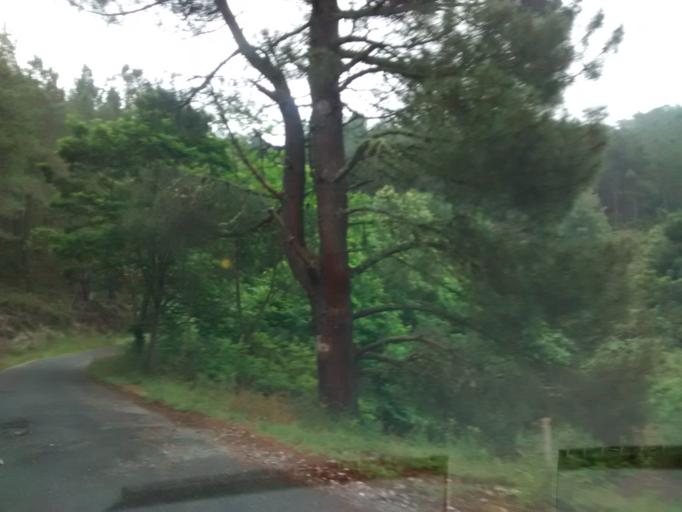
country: ES
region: Galicia
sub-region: Provincia de Ourense
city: Castro Caldelas
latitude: 42.4120
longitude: -7.3904
